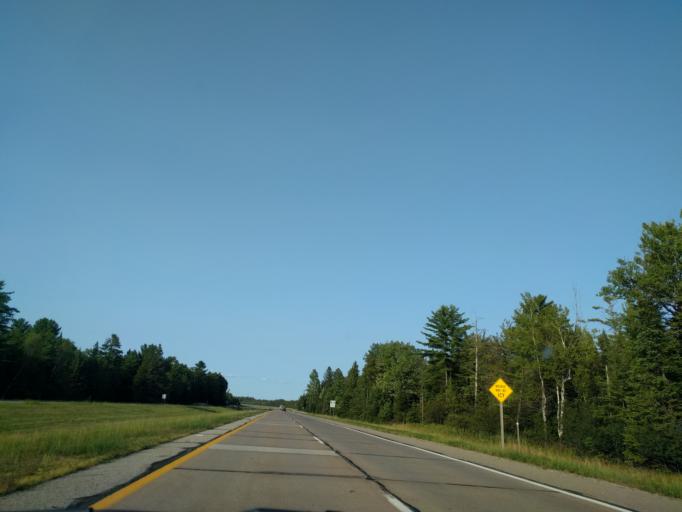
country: US
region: Michigan
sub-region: Delta County
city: Gladstone
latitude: 45.8938
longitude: -87.0001
